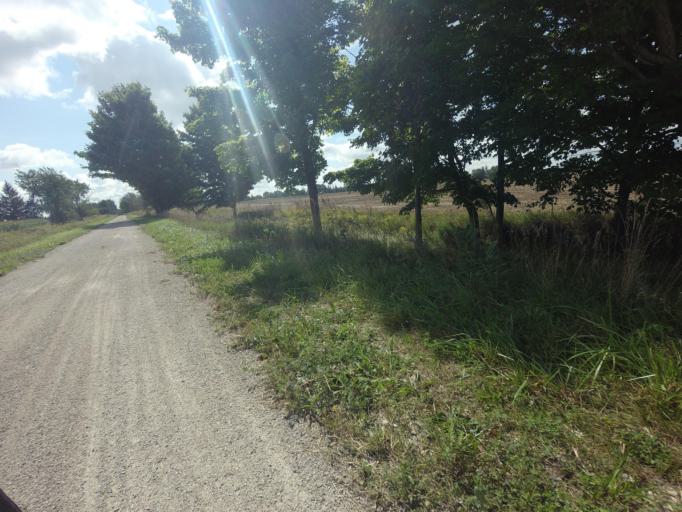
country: CA
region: Ontario
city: Huron East
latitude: 43.6846
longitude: -81.3100
